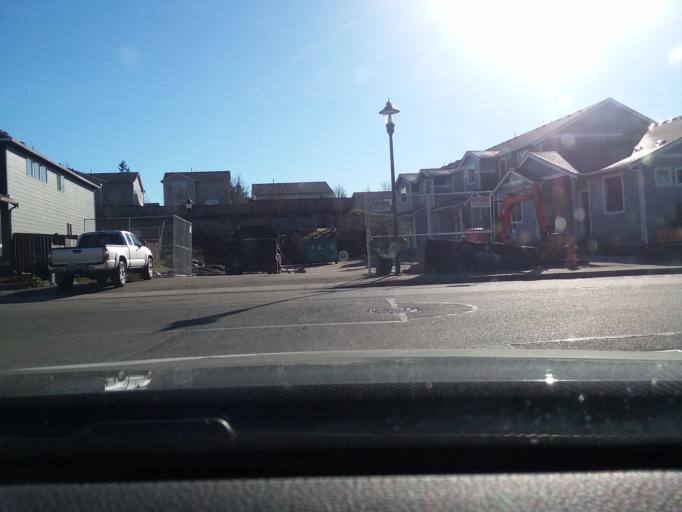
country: US
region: Washington
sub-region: Pierce County
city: Frederickson
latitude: 47.0984
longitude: -122.3184
